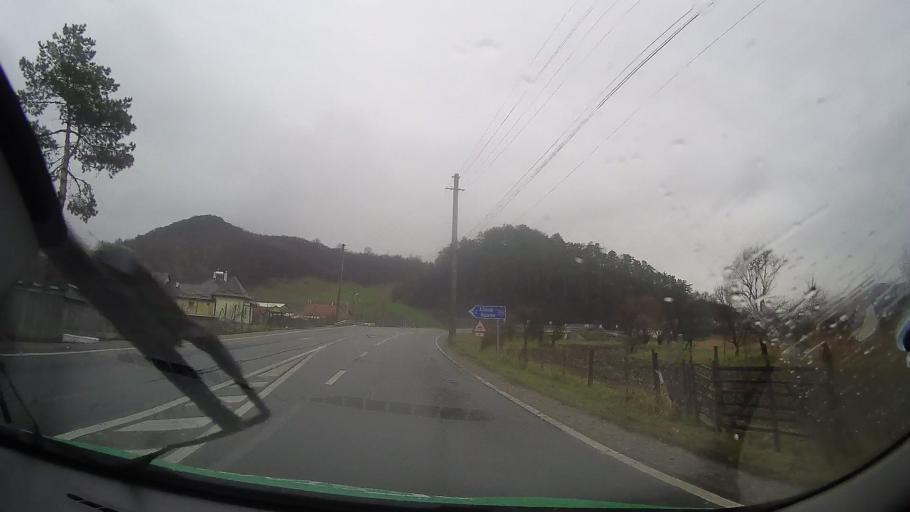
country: RO
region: Bistrita-Nasaud
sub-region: Comuna Galatii Bistritei
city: Galatii Bistritei
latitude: 46.9791
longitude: 24.4362
